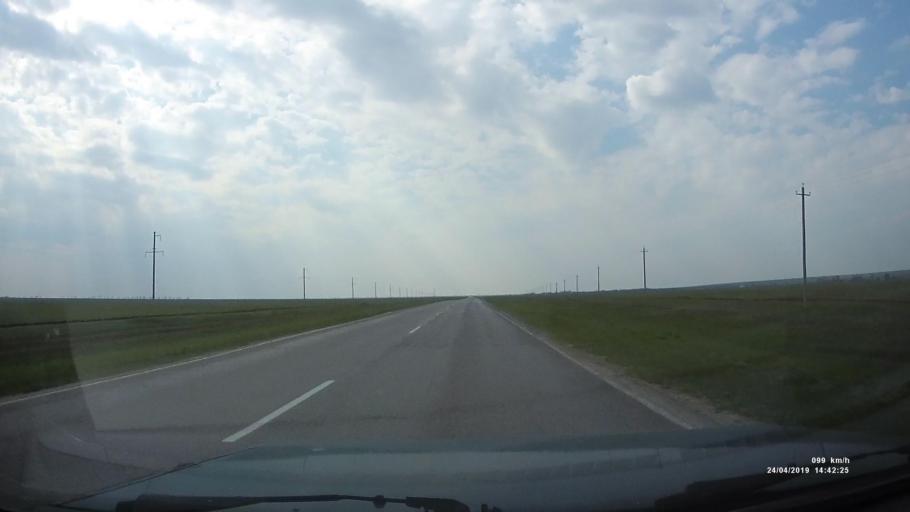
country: RU
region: Rostov
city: Remontnoye
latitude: 46.4518
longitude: 43.8627
